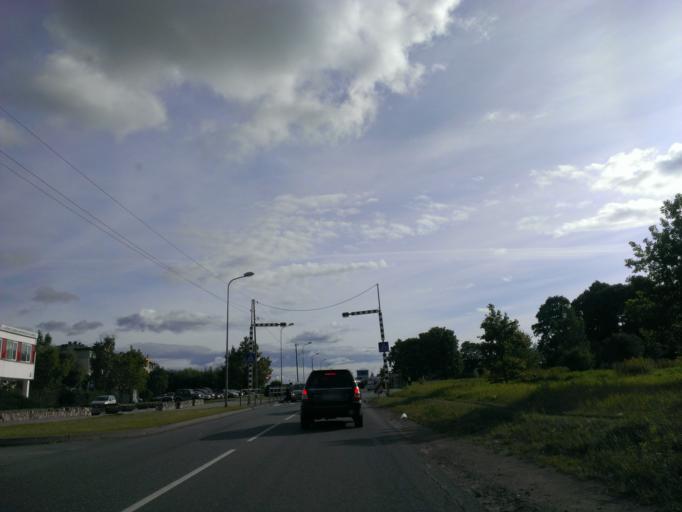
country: LV
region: Stopini
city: Ulbroka
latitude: 56.9596
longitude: 24.2529
